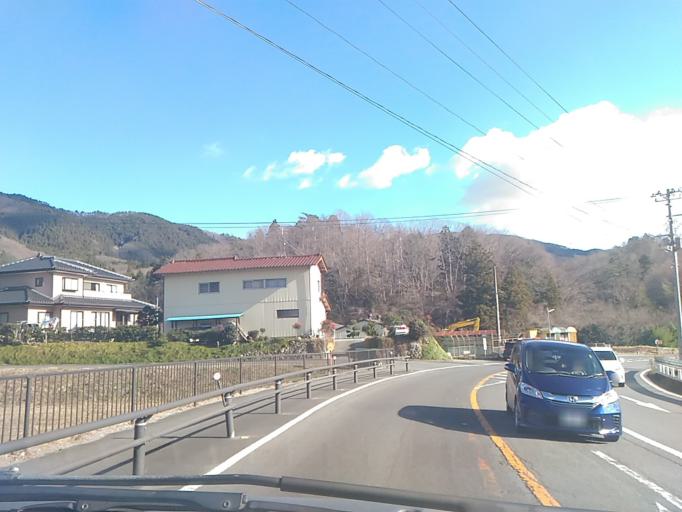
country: JP
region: Fukushima
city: Iwaki
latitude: 37.0166
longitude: 140.7649
